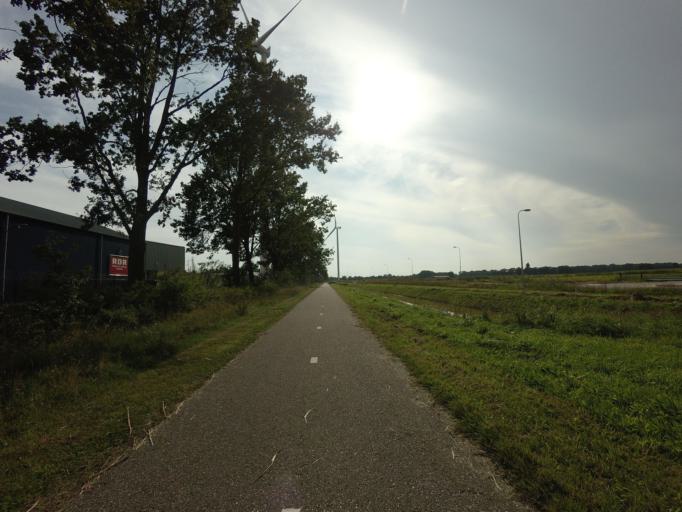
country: NL
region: Drenthe
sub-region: Gemeente Coevorden
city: Coevorden
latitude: 52.6457
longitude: 6.7191
